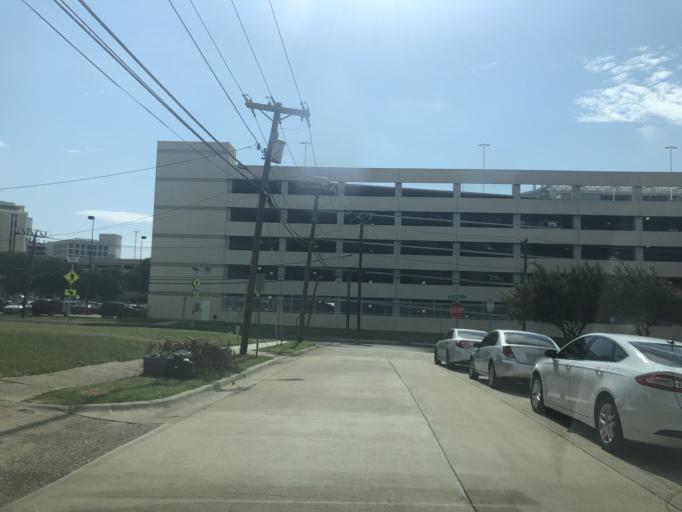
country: US
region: Texas
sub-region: Dallas County
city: Dallas
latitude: 32.8166
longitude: -96.8483
